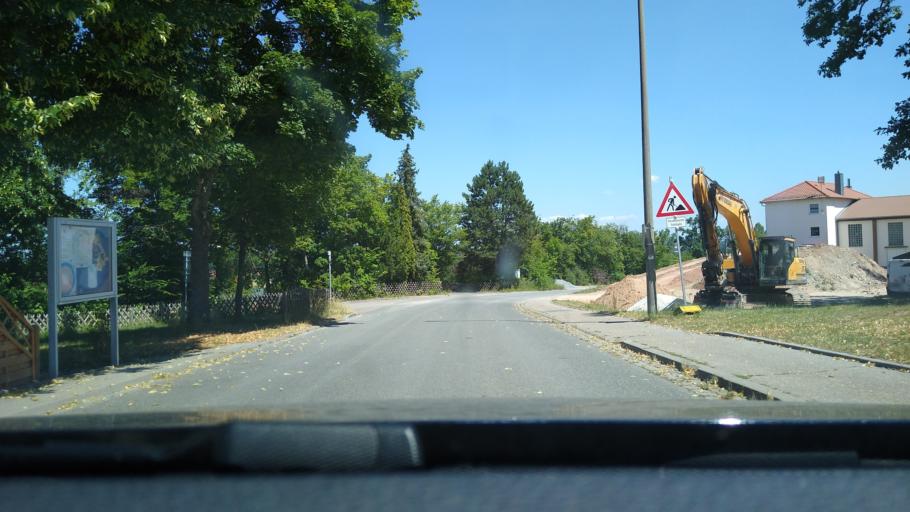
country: DE
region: Bavaria
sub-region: Regierungsbezirk Mittelfranken
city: Cadolzburg
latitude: 49.4614
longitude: 10.8463
